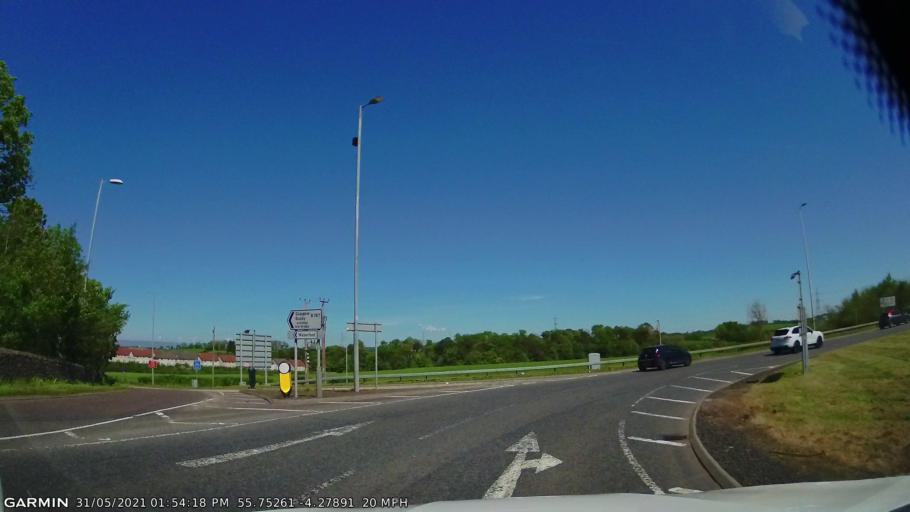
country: GB
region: Scotland
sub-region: East Renfrewshire
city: Eaglesham
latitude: 55.7524
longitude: -4.2789
